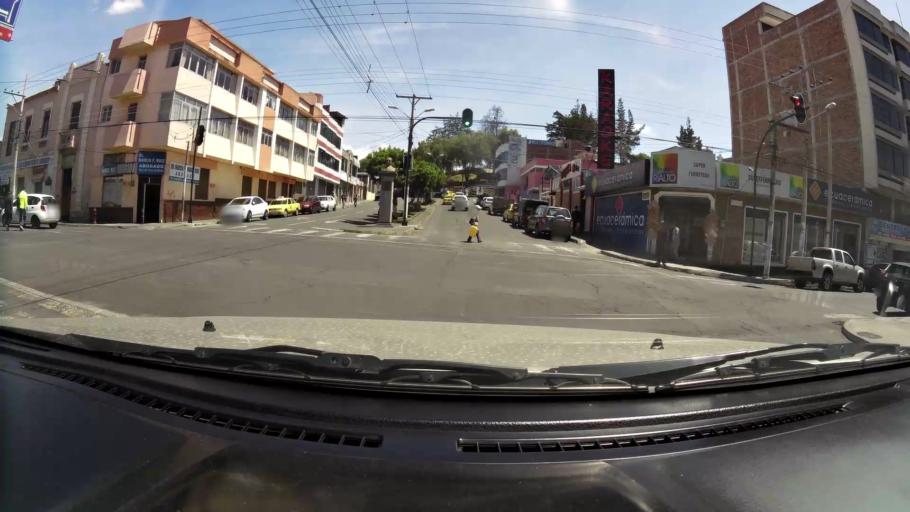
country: EC
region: Chimborazo
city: Riobamba
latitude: -1.6670
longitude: -78.6545
